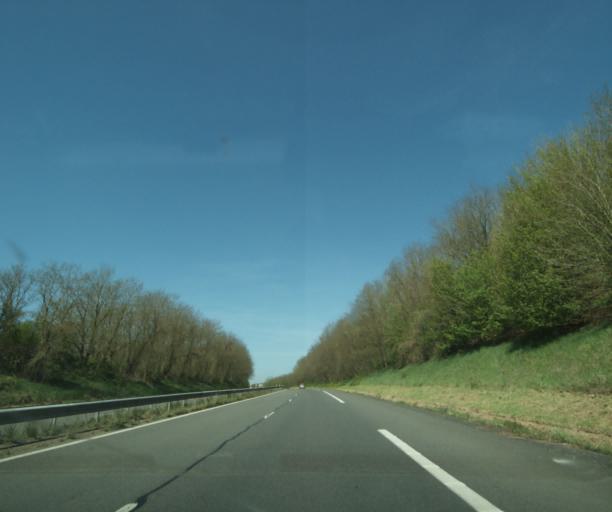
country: FR
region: Bourgogne
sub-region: Departement de la Nievre
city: Chaulgnes
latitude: 47.1104
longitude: 3.0686
